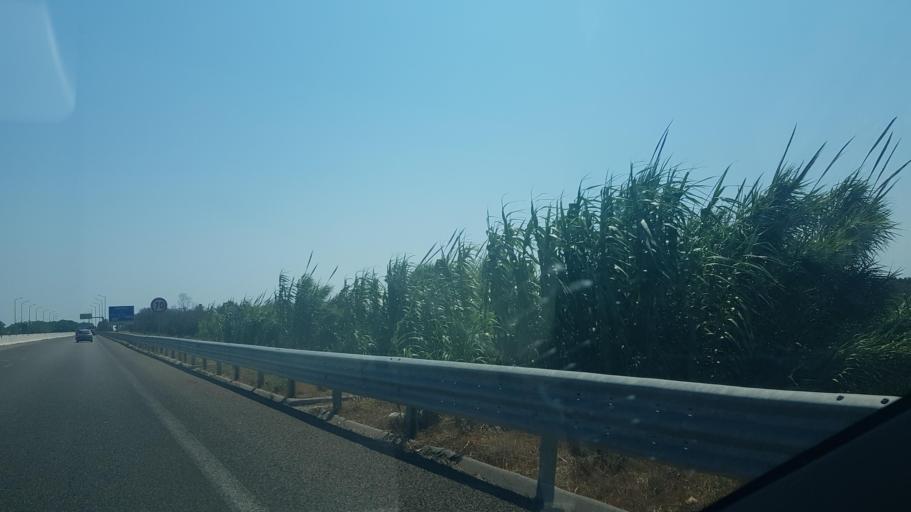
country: IT
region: Apulia
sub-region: Provincia di Lecce
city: Otranto
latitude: 40.1464
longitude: 18.4683
